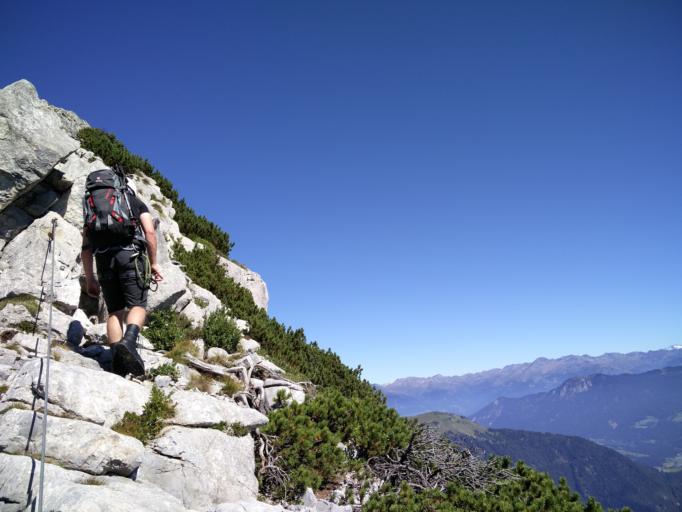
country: IT
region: Friuli Venezia Giulia
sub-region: Provincia di Udine
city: Ravascletto
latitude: 46.6071
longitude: 12.9371
